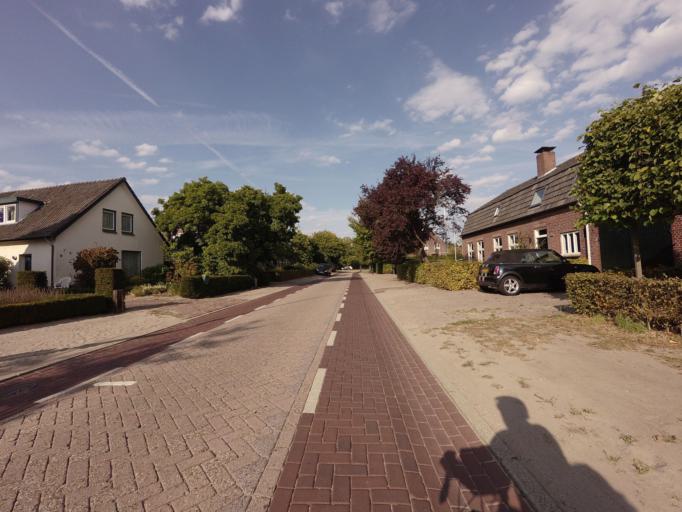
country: NL
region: North Brabant
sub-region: Gemeente Heeze-Leende
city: Heeze
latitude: 51.3439
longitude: 5.5487
